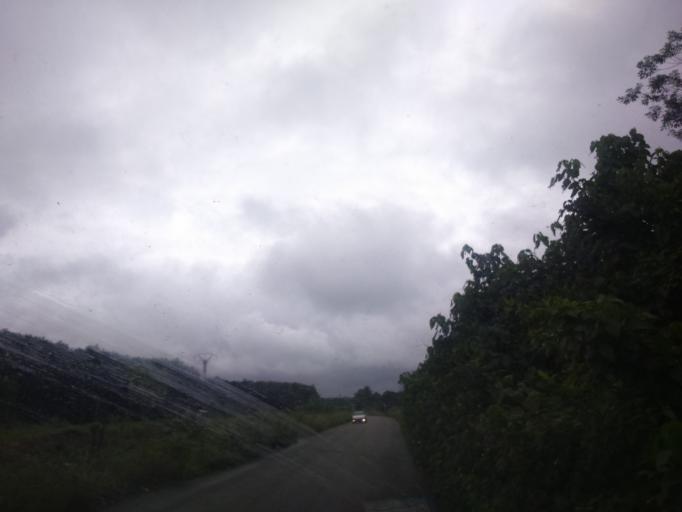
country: CI
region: Sud-Comoe
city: Bonoua
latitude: 5.2818
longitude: -3.4794
